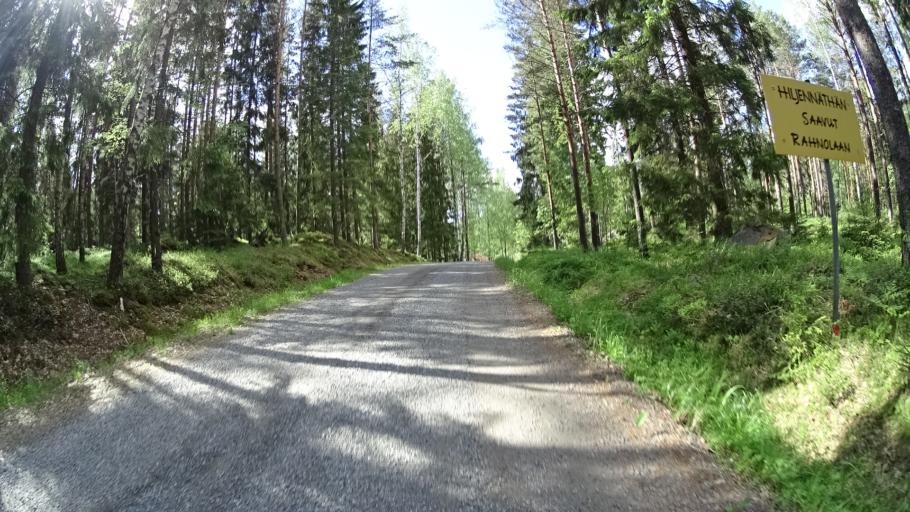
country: FI
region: Varsinais-Suomi
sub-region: Salo
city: Kisko
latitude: 60.1924
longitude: 23.5539
